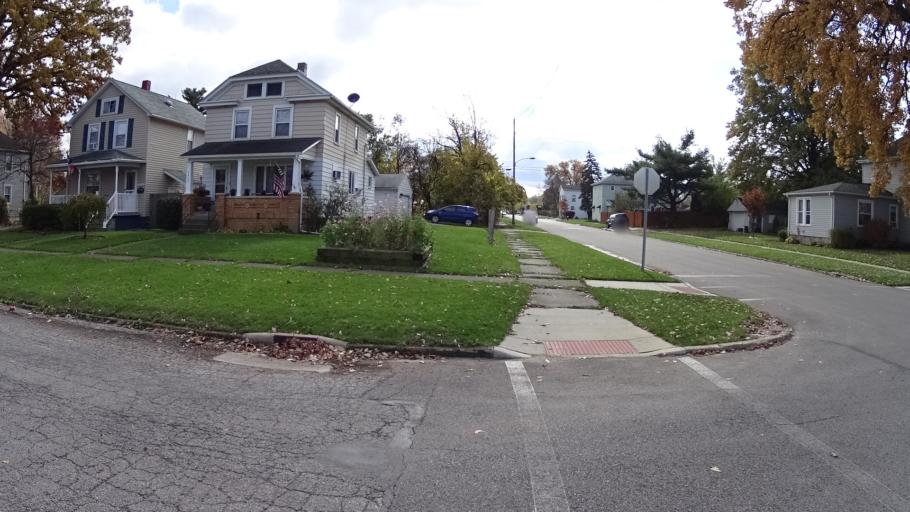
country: US
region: Ohio
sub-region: Lorain County
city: Sheffield
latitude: 41.4448
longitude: -82.1150
